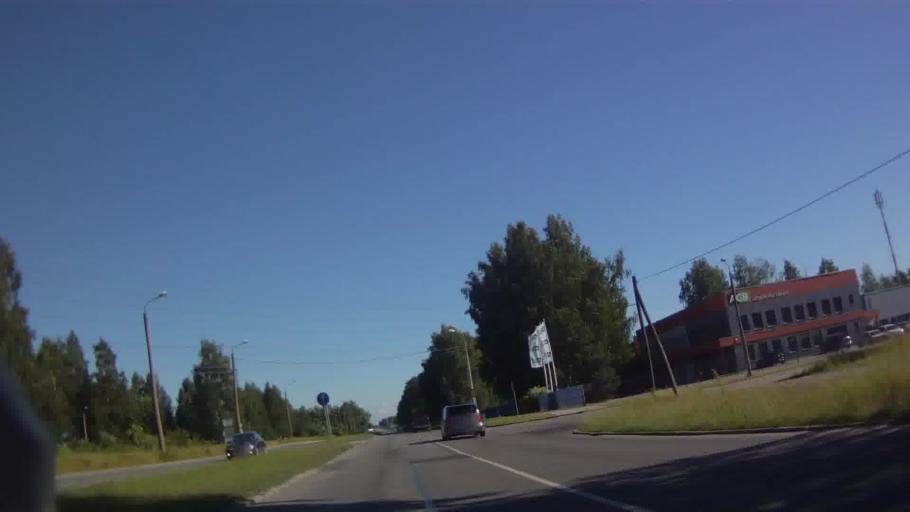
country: LV
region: Kekava
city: Balozi
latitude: 56.9100
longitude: 24.1260
